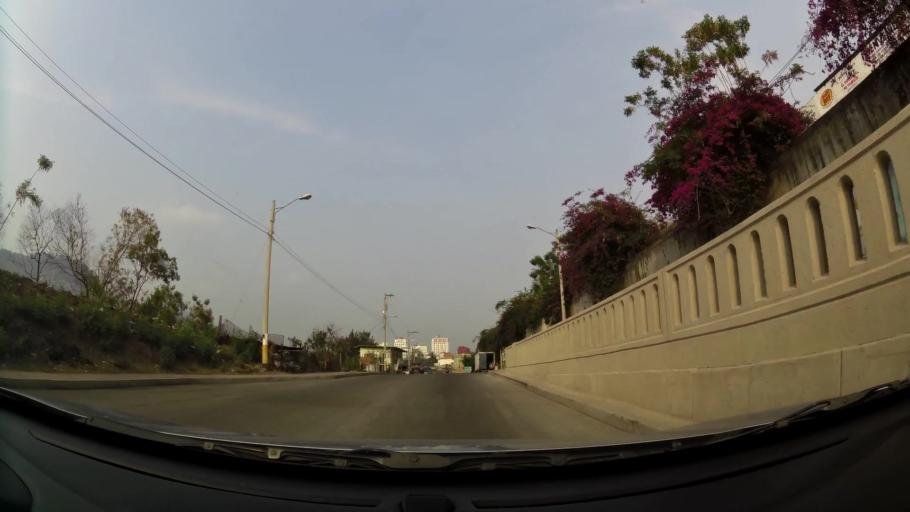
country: HN
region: Francisco Morazan
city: Tegucigalpa
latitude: 14.1012
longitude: -87.2034
